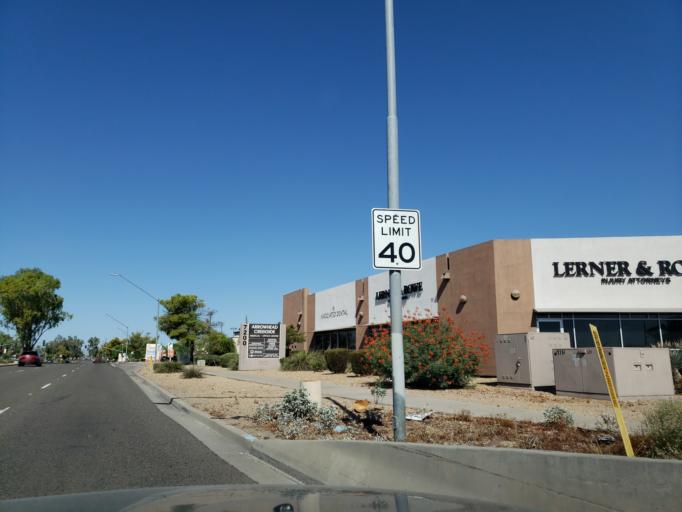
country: US
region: Arizona
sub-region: Maricopa County
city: Peoria
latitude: 33.6385
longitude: -112.2138
